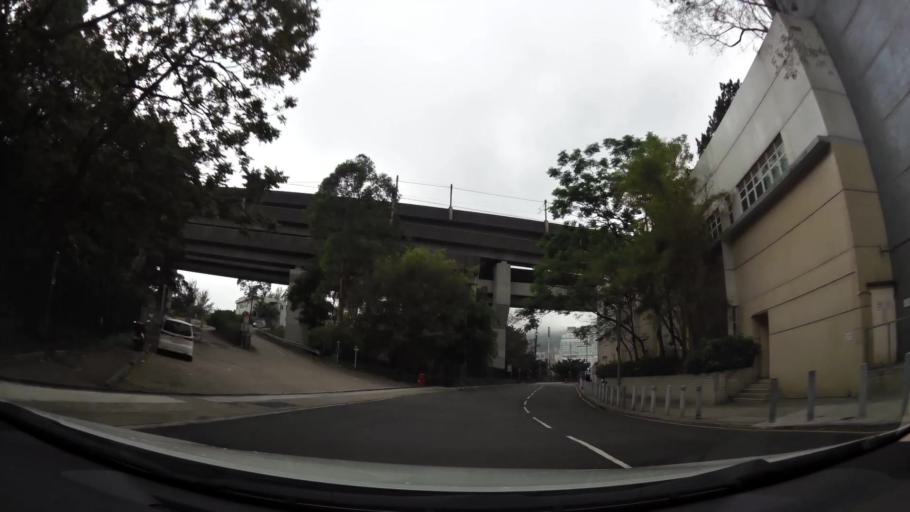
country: HK
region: Tsuen Wan
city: Tsuen Wan
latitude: 22.3554
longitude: 114.1179
